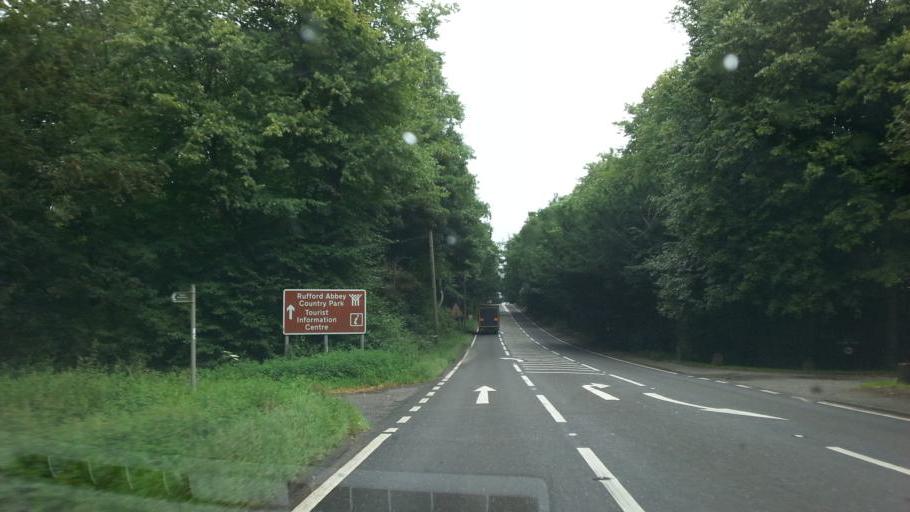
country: GB
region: England
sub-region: Nottinghamshire
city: Edwinstowe
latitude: 53.1725
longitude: -1.0437
